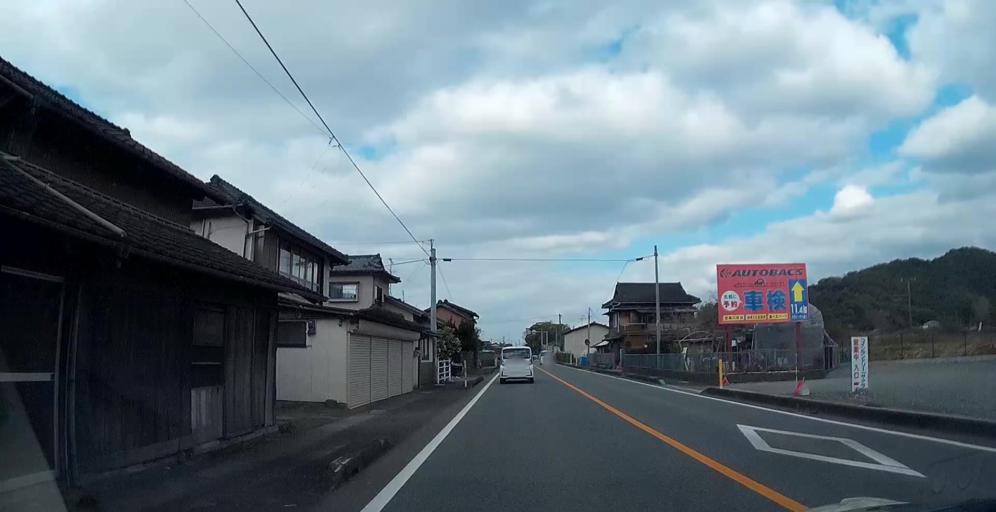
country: JP
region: Kumamoto
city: Yatsushiro
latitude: 32.4425
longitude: 130.5861
